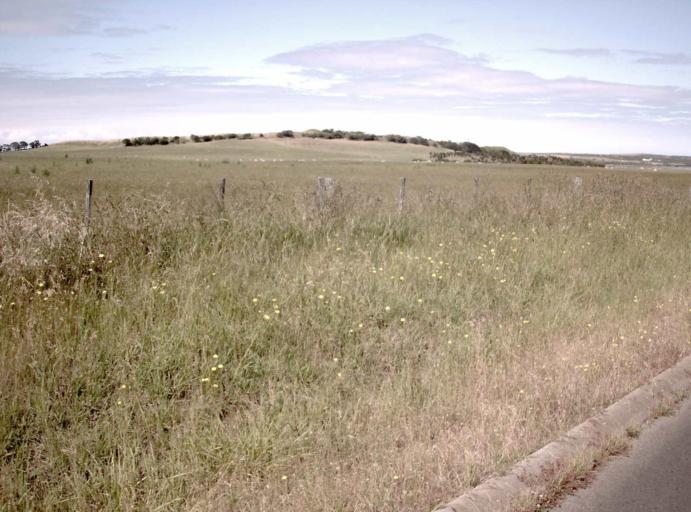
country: AU
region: Victoria
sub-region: Bass Coast
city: Phillip Island
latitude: -38.4966
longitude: 145.1910
